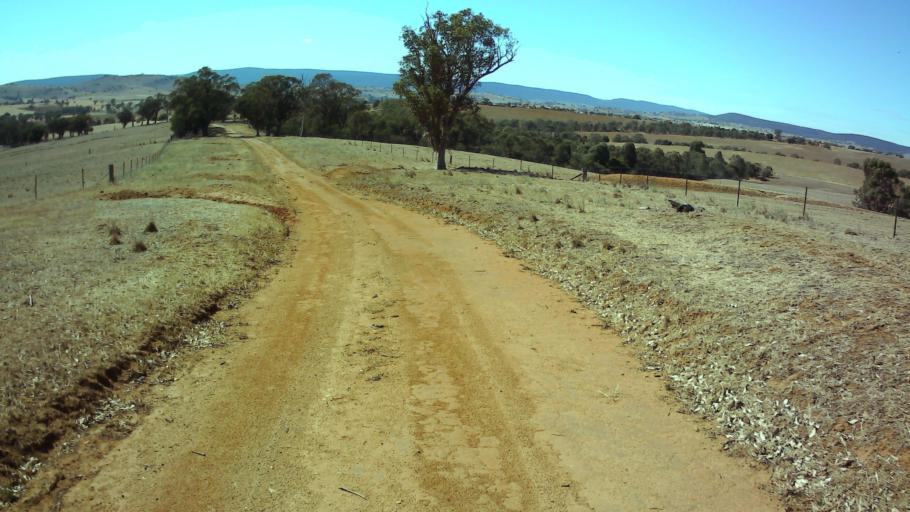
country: AU
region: New South Wales
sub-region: Cowra
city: Cowra
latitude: -33.9772
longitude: 148.4659
